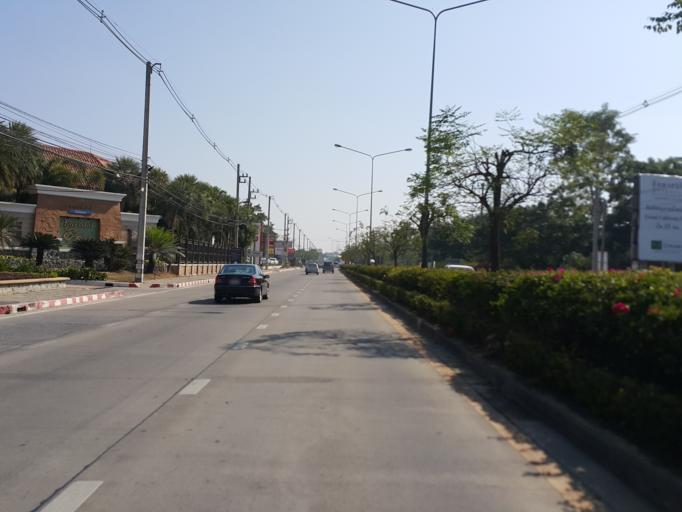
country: TH
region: Chiang Mai
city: Chiang Mai
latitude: 18.7935
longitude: 99.0374
